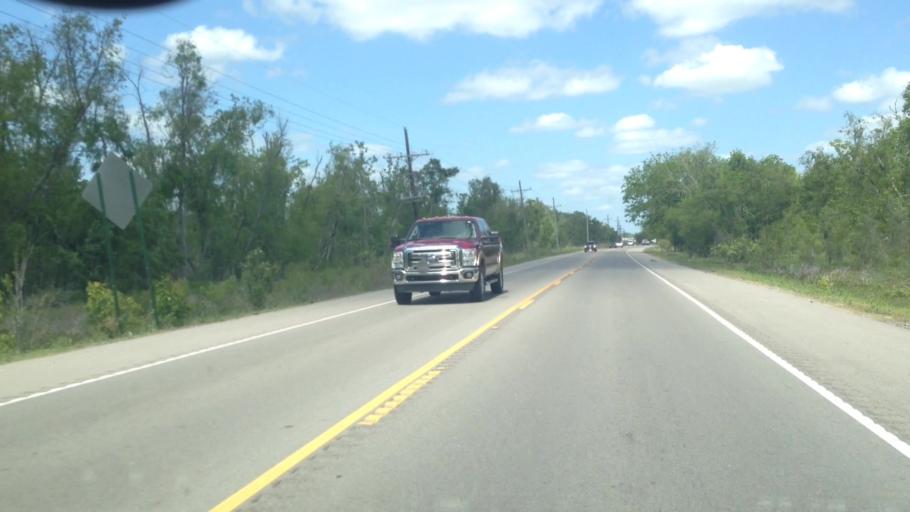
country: US
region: Louisiana
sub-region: Terrebonne Parish
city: Houma
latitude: 29.6347
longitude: -90.7008
